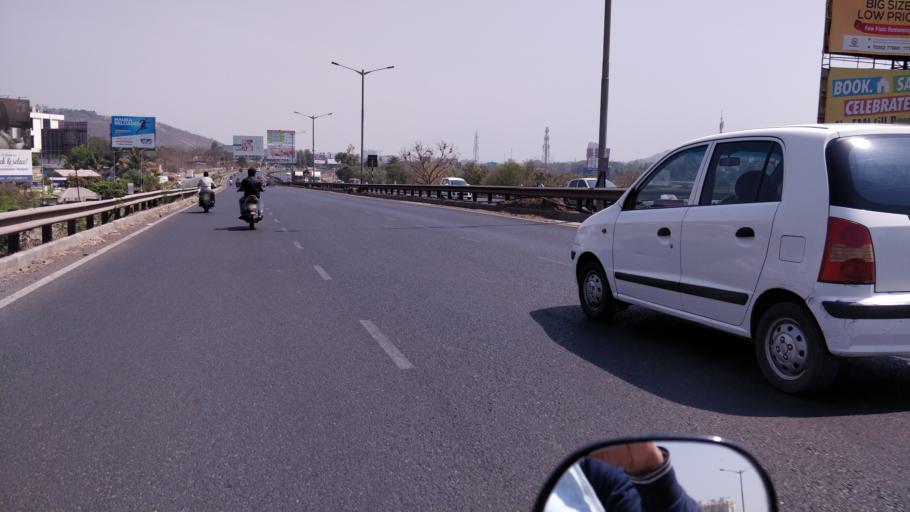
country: IN
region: Maharashtra
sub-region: Pune Division
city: Shivaji Nagar
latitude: 18.5229
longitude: 73.7703
